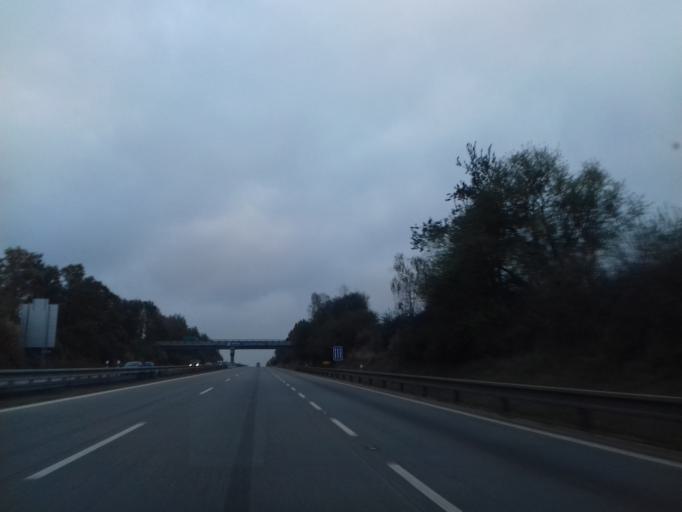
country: CZ
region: Central Bohemia
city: Cechtice
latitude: 49.6500
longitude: 15.1237
